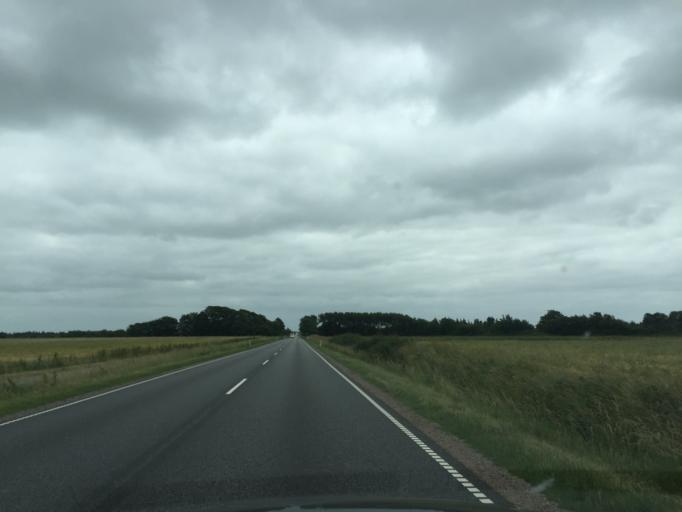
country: DK
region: South Denmark
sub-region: Esbjerg Kommune
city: Ribe
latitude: 55.2599
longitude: 8.7222
